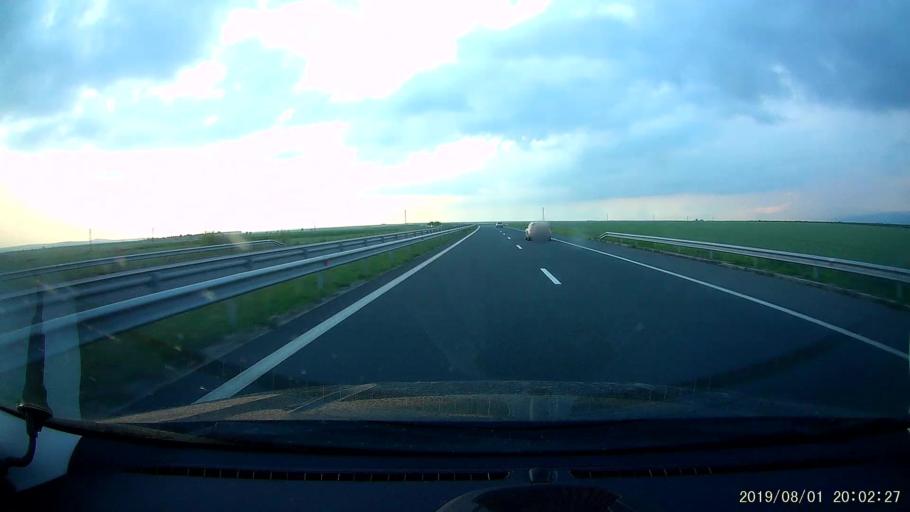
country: BG
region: Yambol
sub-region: Obshtina Straldzha
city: Straldzha
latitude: 42.5598
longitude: 26.6296
